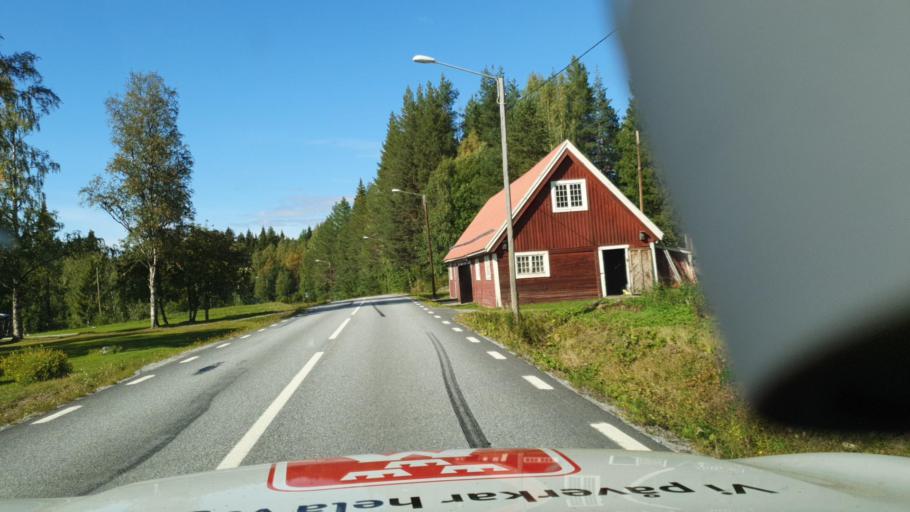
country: SE
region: Vaesterbotten
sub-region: Dorotea Kommun
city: Dorotea
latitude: 64.1167
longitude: 16.2235
